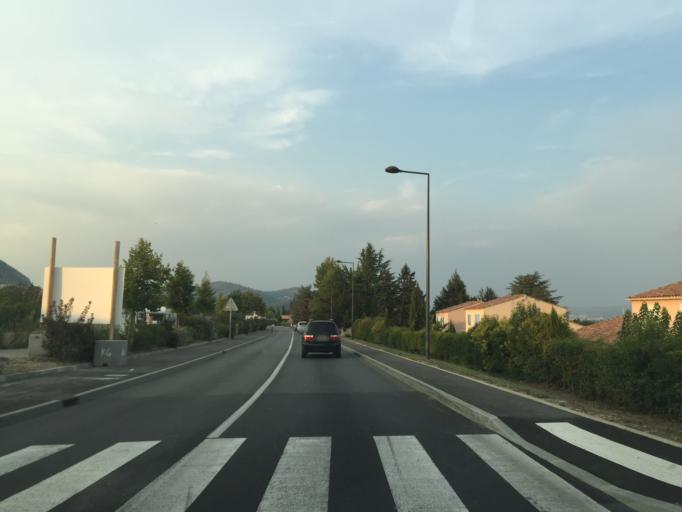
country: FR
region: Provence-Alpes-Cote d'Azur
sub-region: Departement des Alpes-de-Haute-Provence
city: Volx
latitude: 43.8667
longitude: 5.8422
